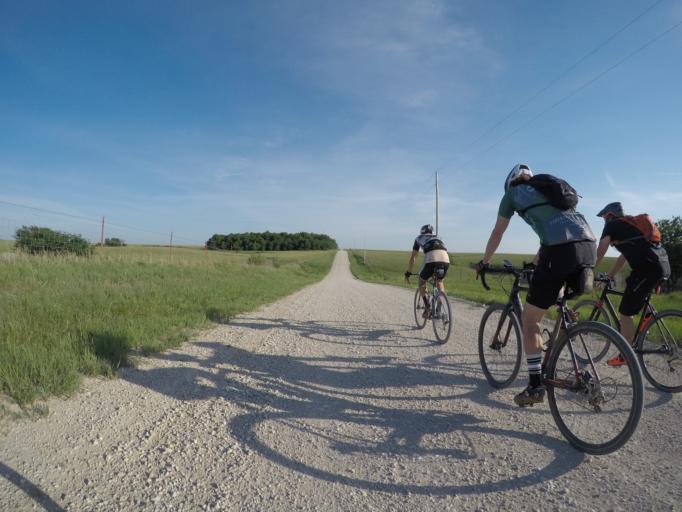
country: US
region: Kansas
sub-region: Riley County
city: Manhattan
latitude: 39.0172
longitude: -96.4918
